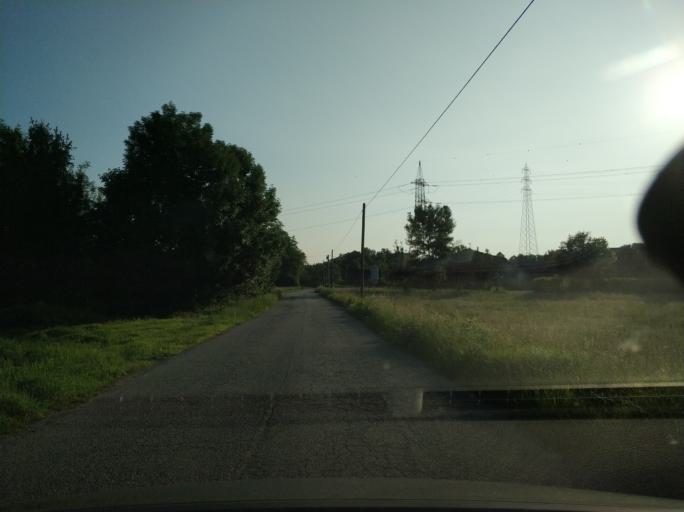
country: IT
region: Piedmont
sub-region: Provincia di Torino
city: Cafasse
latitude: 45.2440
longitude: 7.5285
